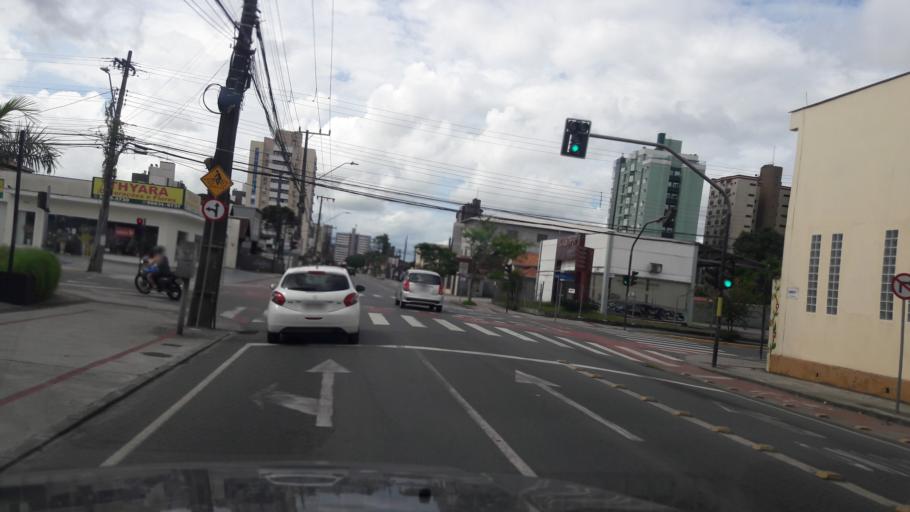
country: BR
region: Santa Catarina
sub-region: Joinville
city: Joinville
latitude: -26.3149
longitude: -48.8427
